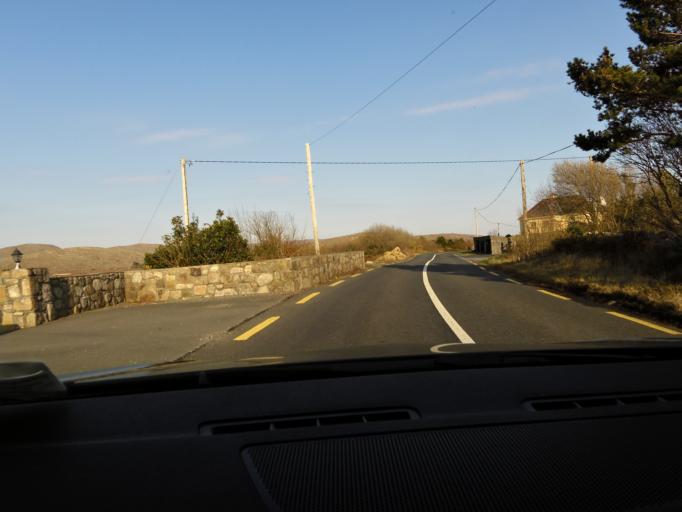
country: IE
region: Connaught
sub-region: County Galway
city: Oughterard
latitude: 53.3920
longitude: -9.6450
